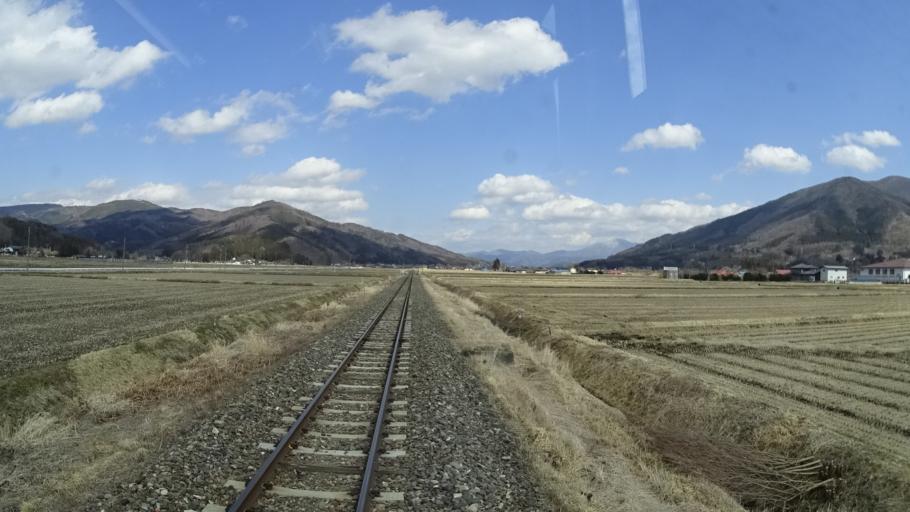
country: JP
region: Iwate
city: Tono
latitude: 39.3254
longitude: 141.4633
